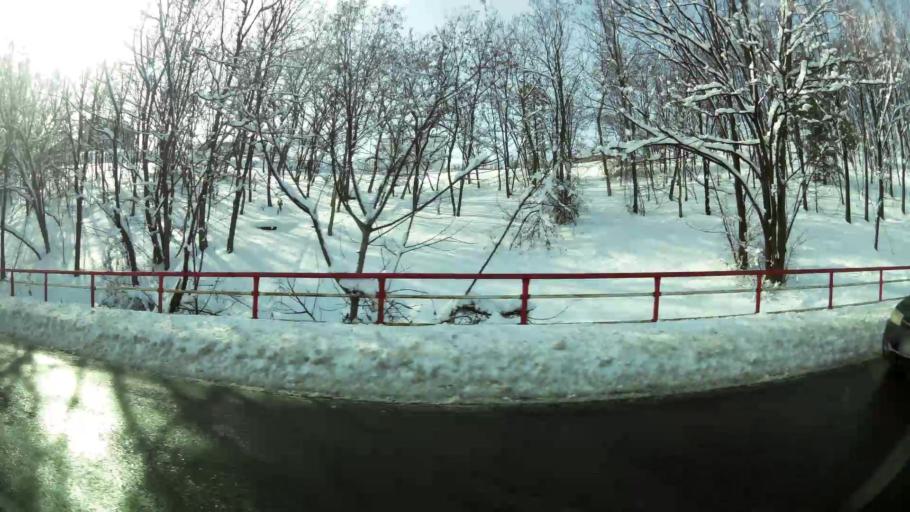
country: RS
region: Central Serbia
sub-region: Belgrade
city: Zvezdara
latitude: 44.7885
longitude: 20.5269
